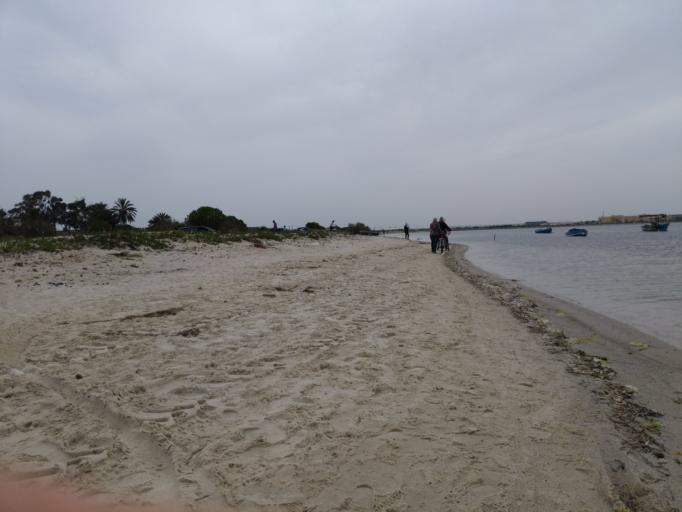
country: TN
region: Al Munastir
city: Saqanis
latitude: 35.7772
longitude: 10.7780
